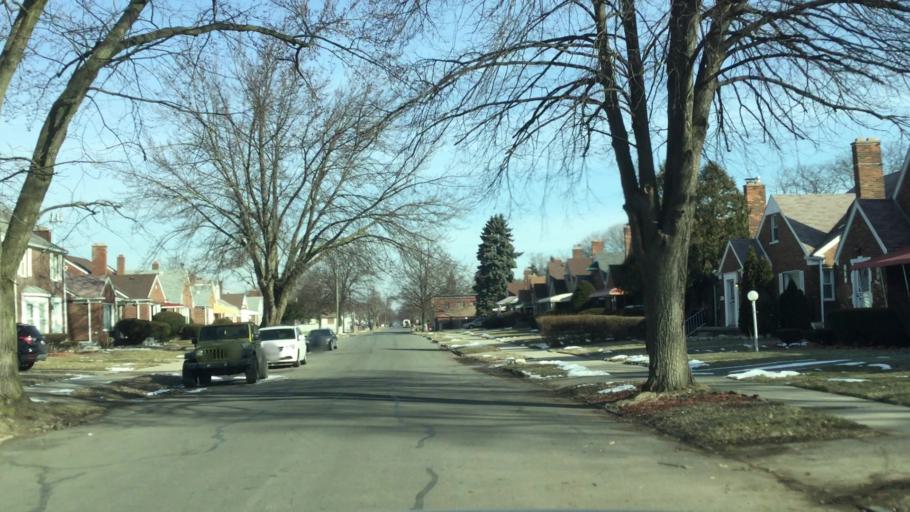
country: US
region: Michigan
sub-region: Wayne County
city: Dearborn
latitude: 42.3568
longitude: -83.1762
